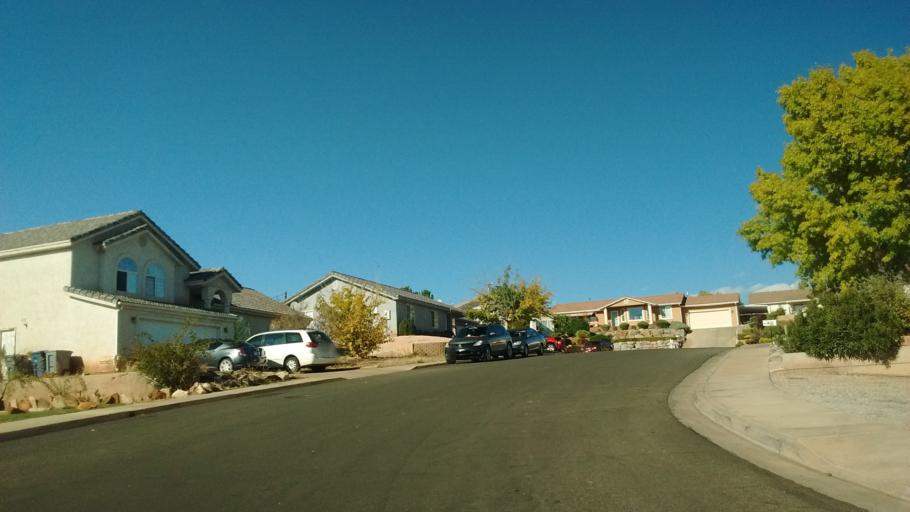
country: US
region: Utah
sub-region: Washington County
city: Washington
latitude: 37.1384
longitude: -113.4997
